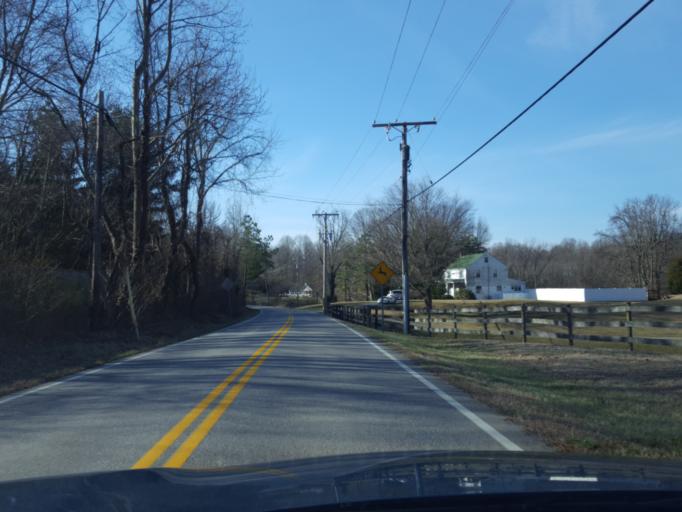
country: US
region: Maryland
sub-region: Calvert County
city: Prince Frederick
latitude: 38.5993
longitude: -76.5263
